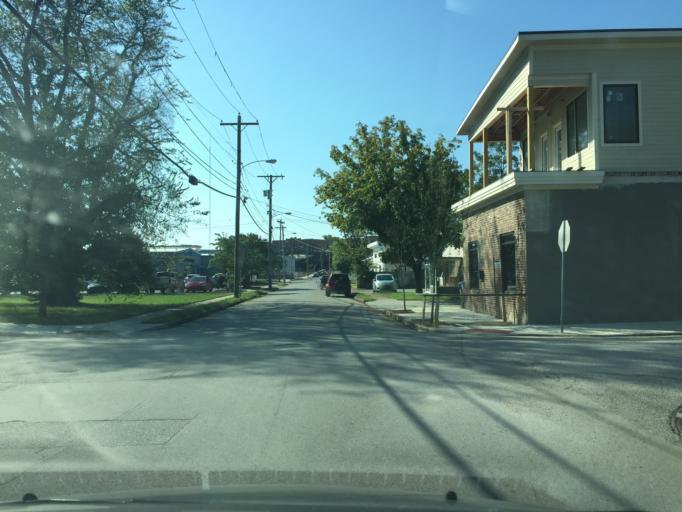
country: US
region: Tennessee
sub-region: Hamilton County
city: Chattanooga
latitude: 35.0670
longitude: -85.3103
